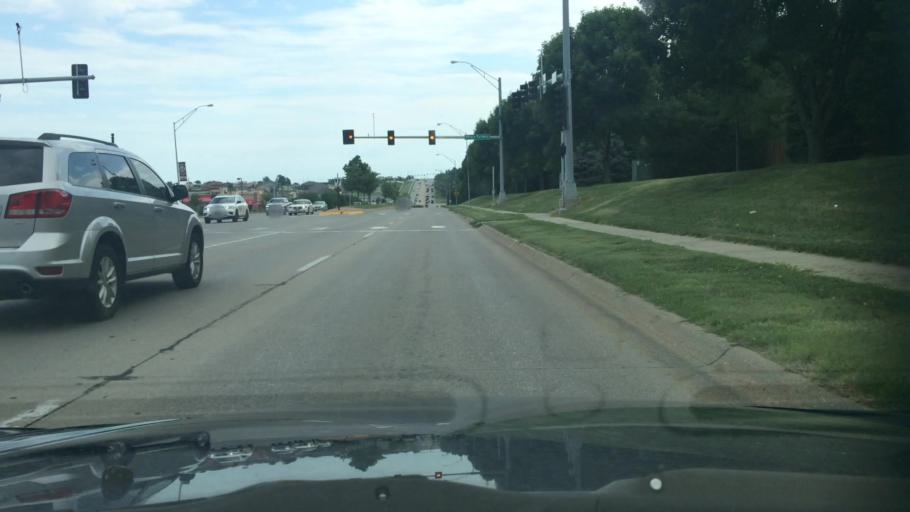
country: US
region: Nebraska
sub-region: Sarpy County
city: La Vista
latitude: 41.1734
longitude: -96.0238
